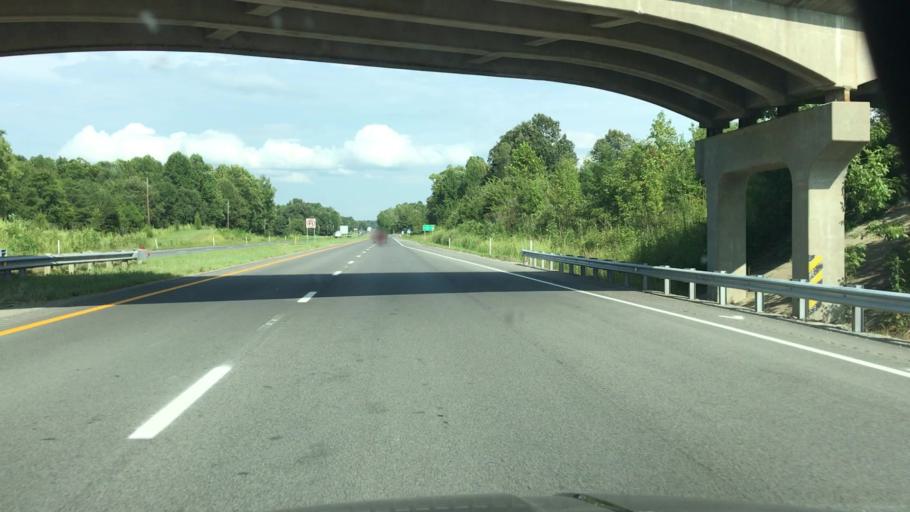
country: US
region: Kentucky
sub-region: Hopkins County
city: Nortonville
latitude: 37.2123
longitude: -87.4344
